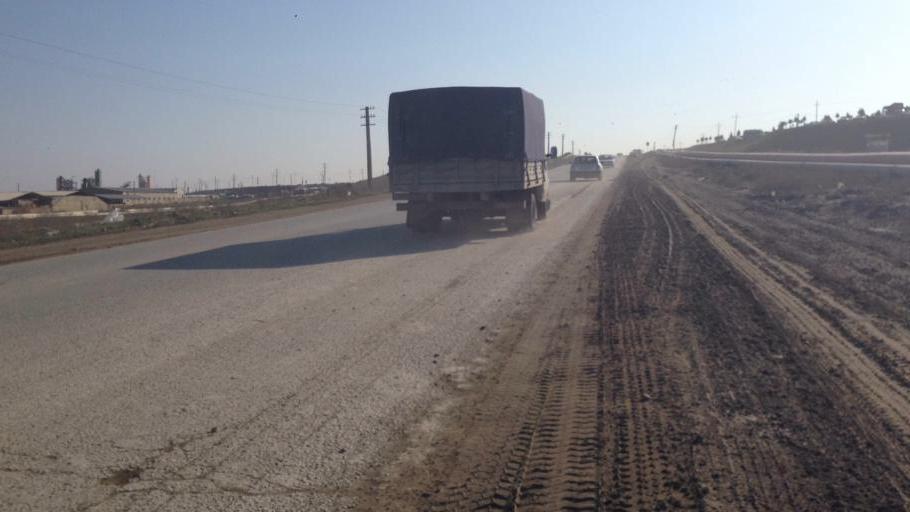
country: AZ
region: Abseron
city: Digah
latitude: 40.4655
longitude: 49.8876
